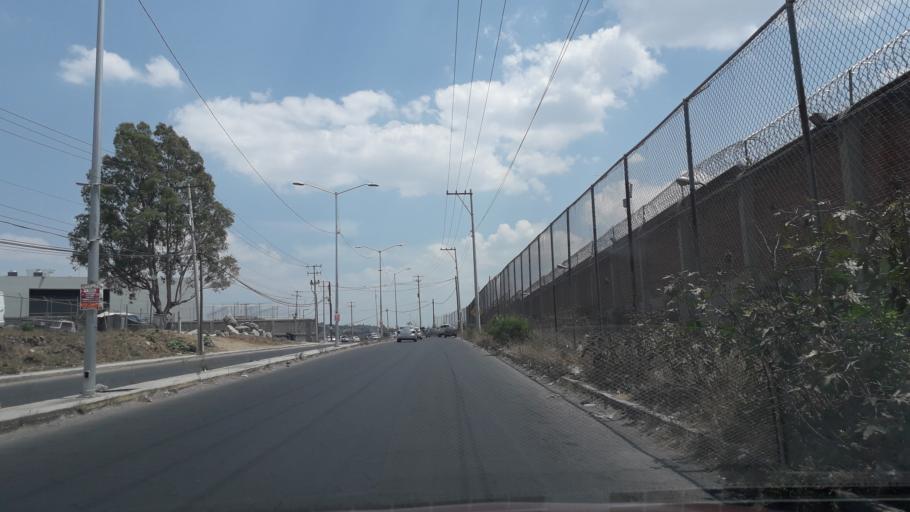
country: MX
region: Puebla
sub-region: Puebla
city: Galaxia la Calera
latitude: 18.9927
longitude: -98.1722
